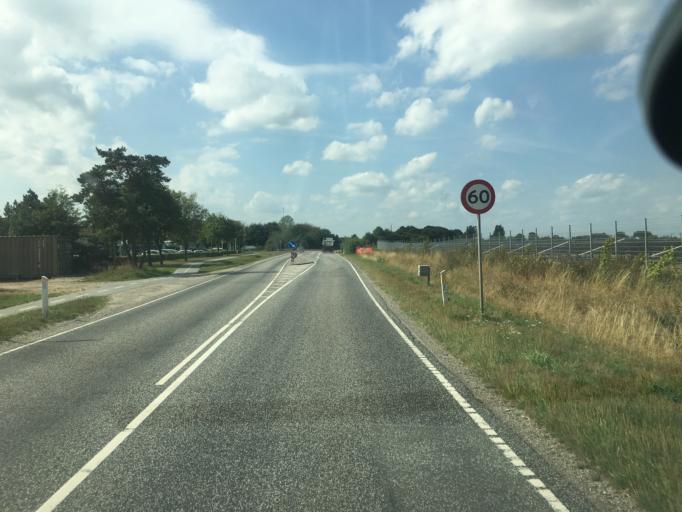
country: DK
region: South Denmark
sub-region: Aabenraa Kommune
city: Tinglev
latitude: 54.9423
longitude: 9.2666
